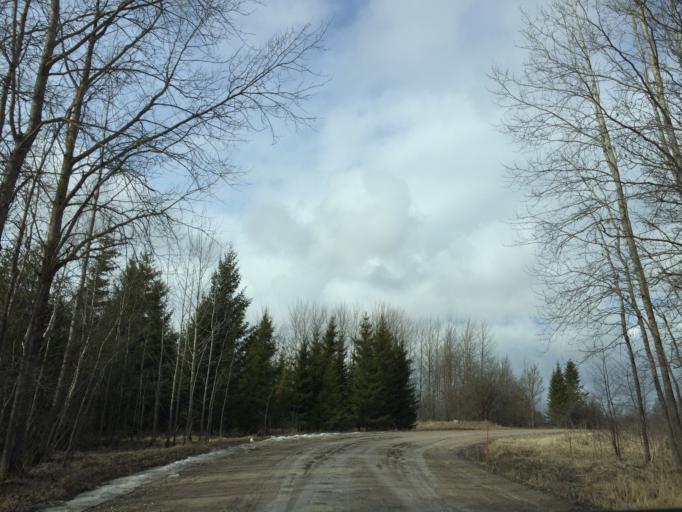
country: EE
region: Laeaene
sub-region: Lihula vald
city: Lihula
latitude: 58.7334
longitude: 23.8288
